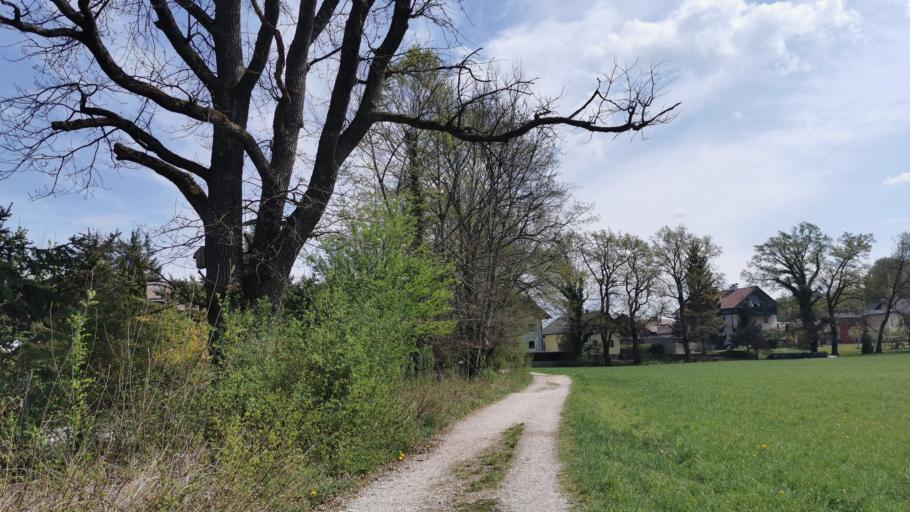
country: AT
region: Salzburg
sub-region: Politischer Bezirk Salzburg-Umgebung
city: Grodig
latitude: 47.7513
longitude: 13.0112
